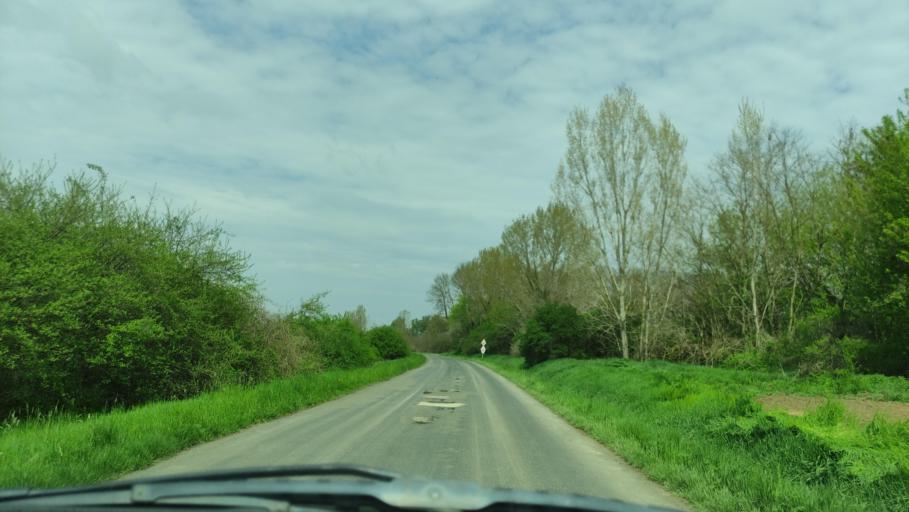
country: HU
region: Baranya
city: Magocs
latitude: 46.2955
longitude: 18.1815
